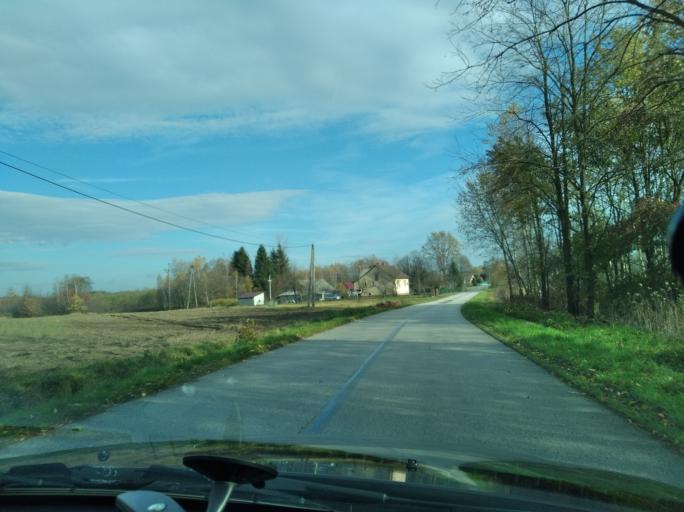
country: PL
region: Subcarpathian Voivodeship
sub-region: Powiat ropczycko-sedziszowski
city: Sedziszow Malopolski
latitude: 50.1036
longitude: 21.6766
